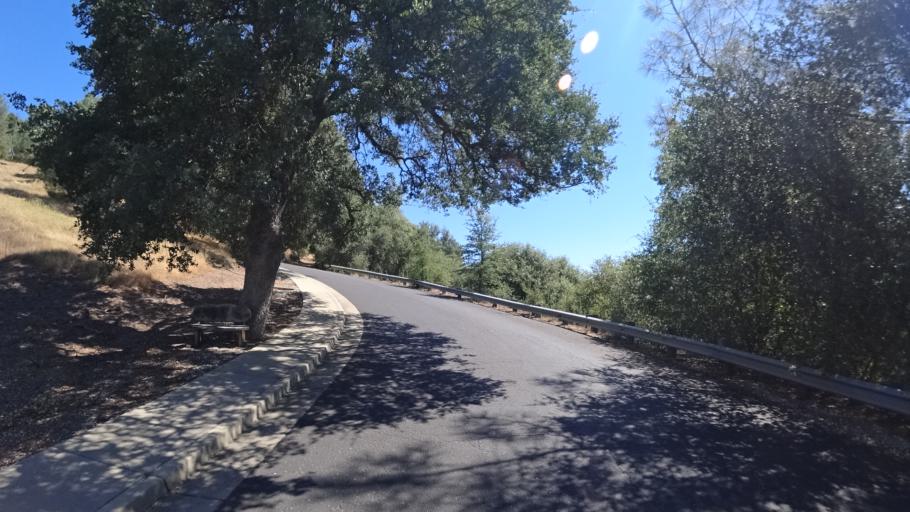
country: US
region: California
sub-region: Calaveras County
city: Angels Camp
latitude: 38.0758
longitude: -120.5352
